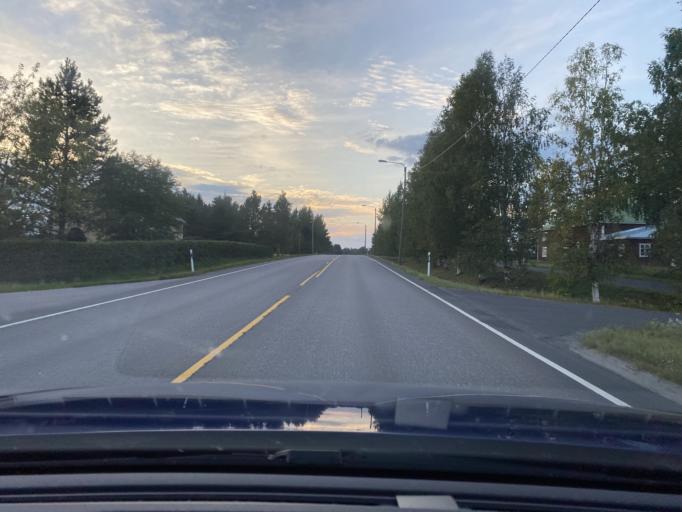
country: FI
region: Satakunta
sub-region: Pohjois-Satakunta
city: Kankaanpaeae
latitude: 61.7466
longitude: 22.5213
